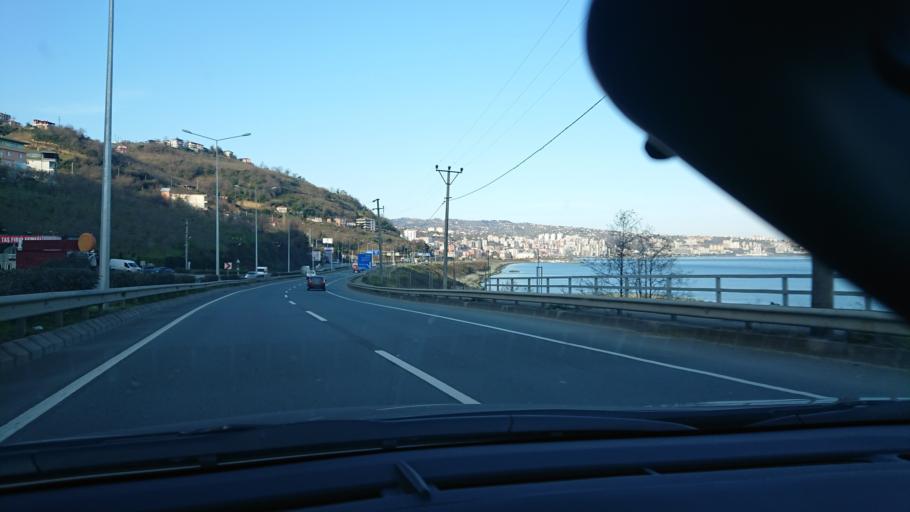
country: TR
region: Trabzon
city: Yomra
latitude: 40.9537
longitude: 39.8875
